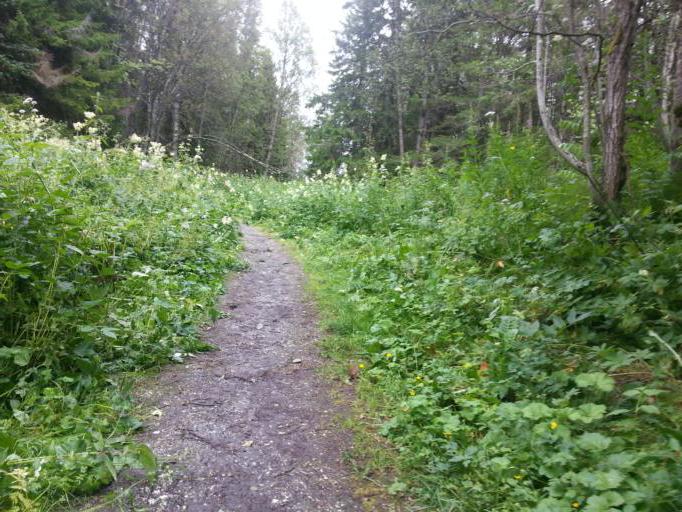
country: NO
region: Troms
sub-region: Tromso
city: Tromso
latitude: 69.6338
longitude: 18.9127
